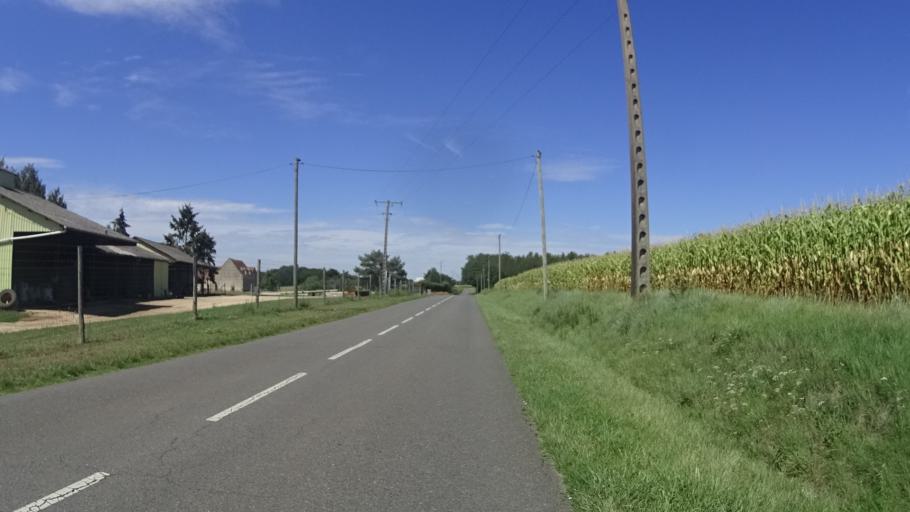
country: FR
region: Centre
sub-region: Departement du Loiret
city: Briare
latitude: 47.6152
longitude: 2.7558
